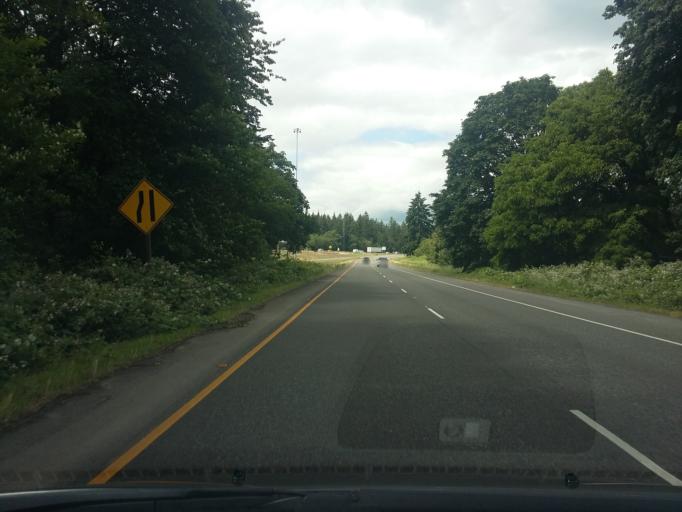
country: US
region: Washington
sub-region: Clark County
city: Orchards
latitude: 45.6061
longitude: -122.5495
